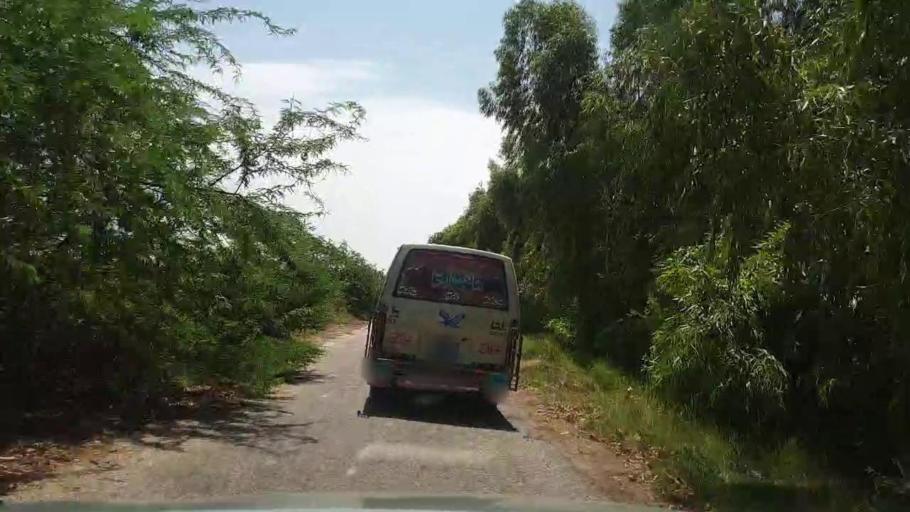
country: PK
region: Sindh
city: Bozdar
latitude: 27.0701
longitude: 68.9782
